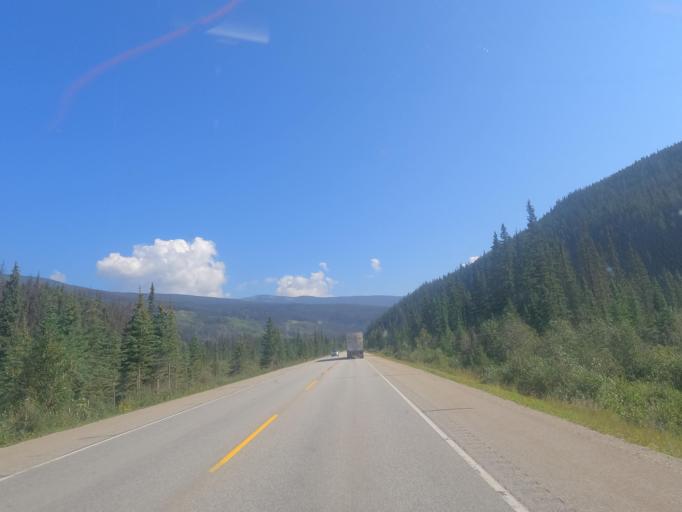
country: CA
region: Alberta
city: Jasper Park Lodge
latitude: 52.8816
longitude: -118.4889
